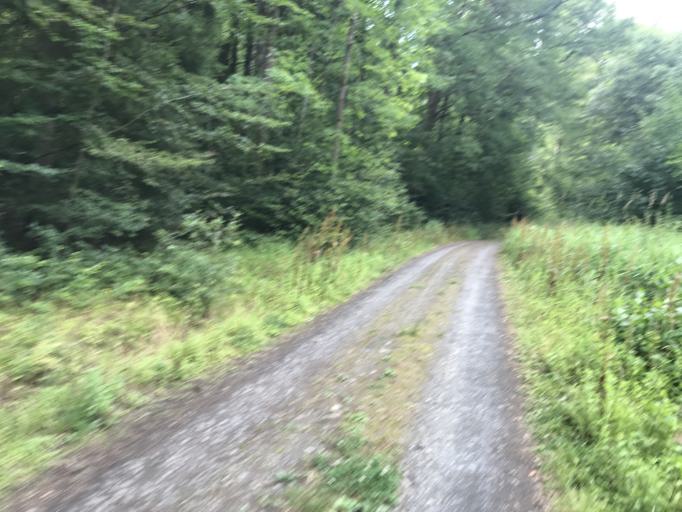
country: DE
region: Hesse
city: Lollar
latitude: 50.6438
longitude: 8.6447
